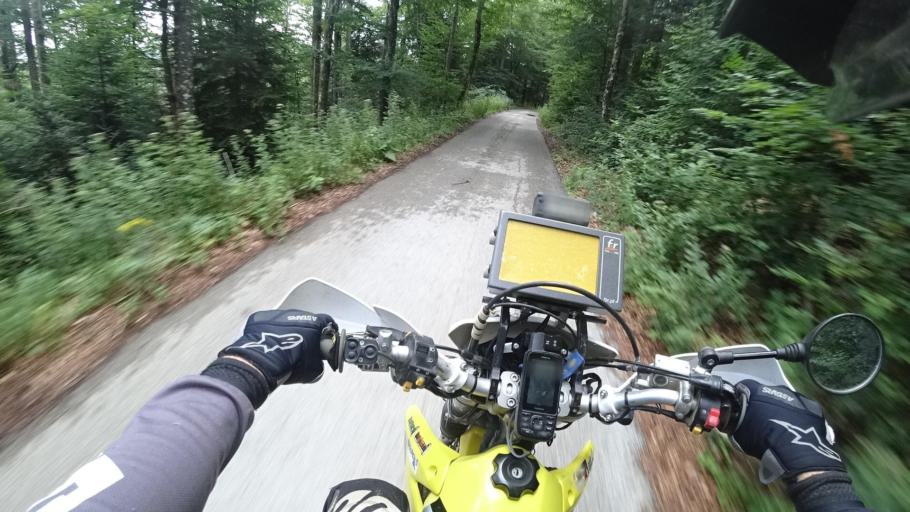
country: HR
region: Licko-Senjska
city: Senj
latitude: 45.1141
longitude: 14.9453
